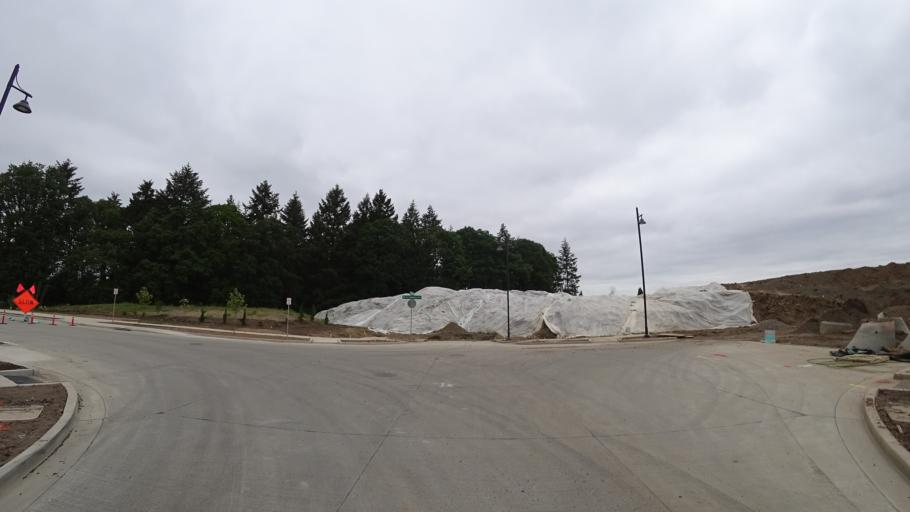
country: US
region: Oregon
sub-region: Washington County
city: Aloha
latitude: 45.4906
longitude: -122.9172
